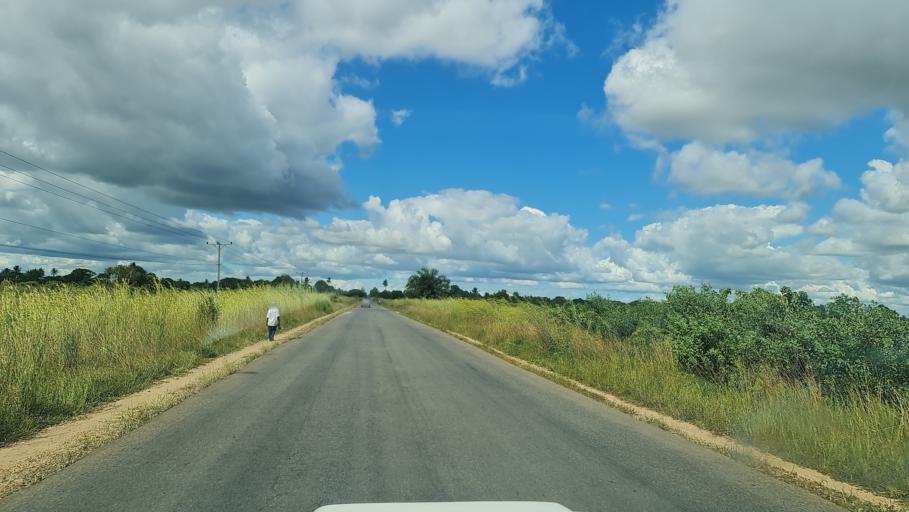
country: MZ
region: Zambezia
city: Quelimane
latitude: -17.5934
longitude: 36.7750
